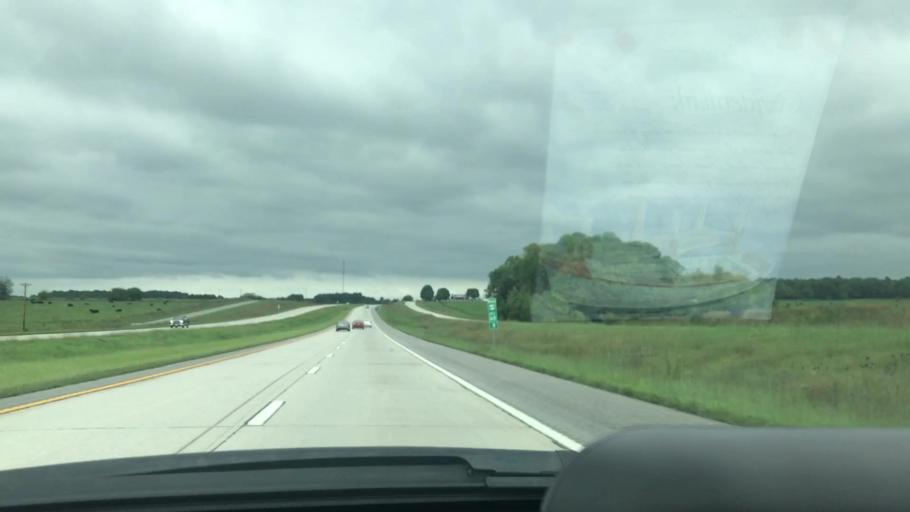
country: US
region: Missouri
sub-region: Greene County
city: Fair Grove
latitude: 37.4403
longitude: -93.1446
